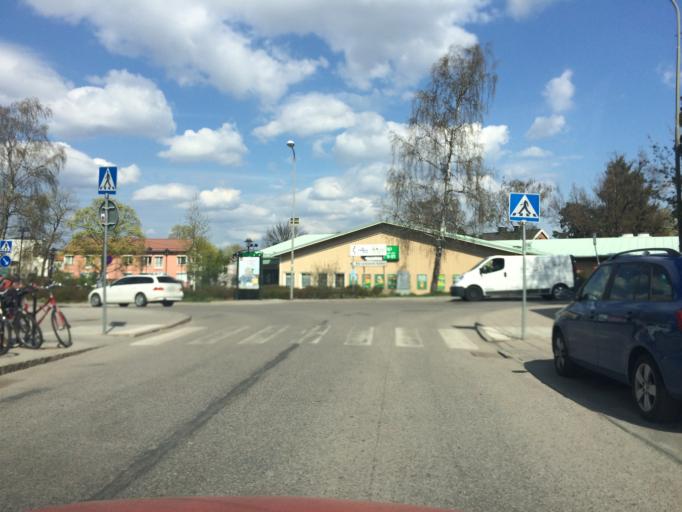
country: SE
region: Stockholm
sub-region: Huddinge Kommun
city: Segeltorp
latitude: 59.3008
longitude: 17.9572
